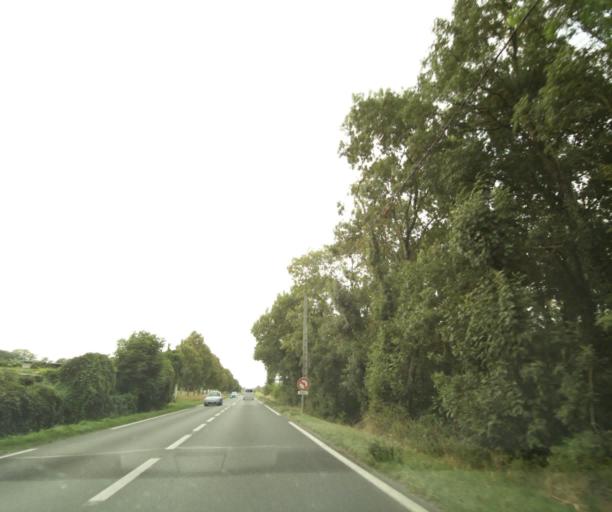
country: FR
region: Centre
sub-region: Departement d'Indre-et-Loire
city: Perrusson
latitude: 47.0777
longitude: 1.0536
